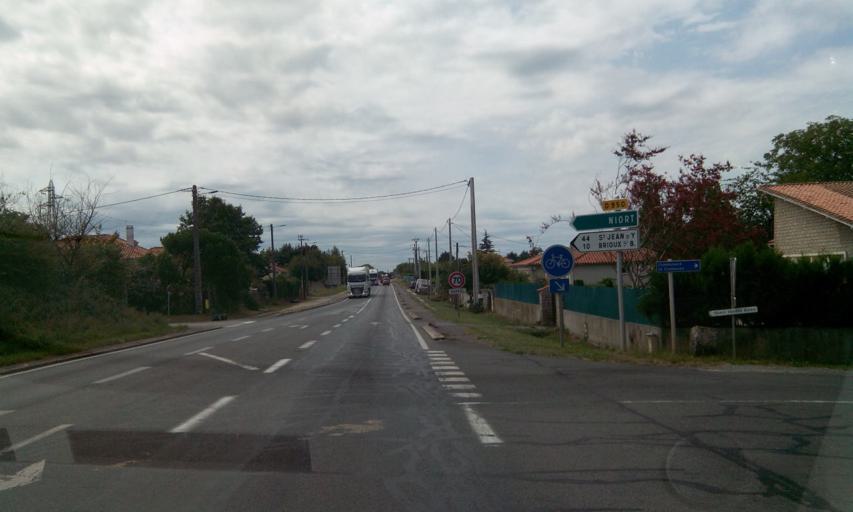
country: FR
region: Poitou-Charentes
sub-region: Departement des Deux-Sevres
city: Melle
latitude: 46.2152
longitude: -0.1418
